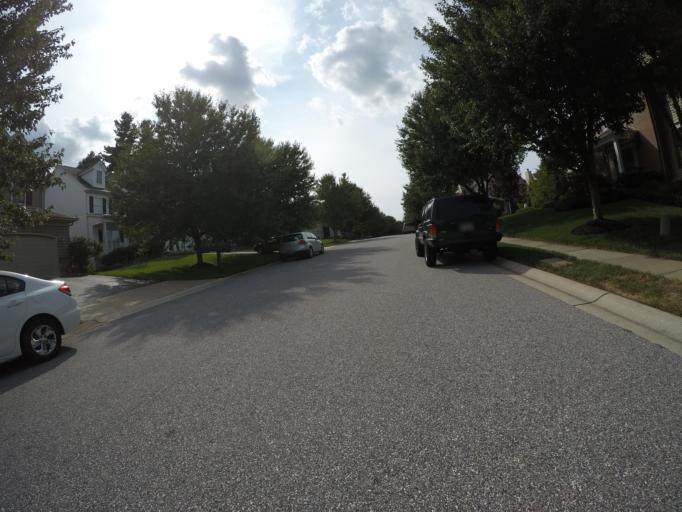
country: US
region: Maryland
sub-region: Howard County
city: Columbia
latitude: 39.3119
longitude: -76.8857
